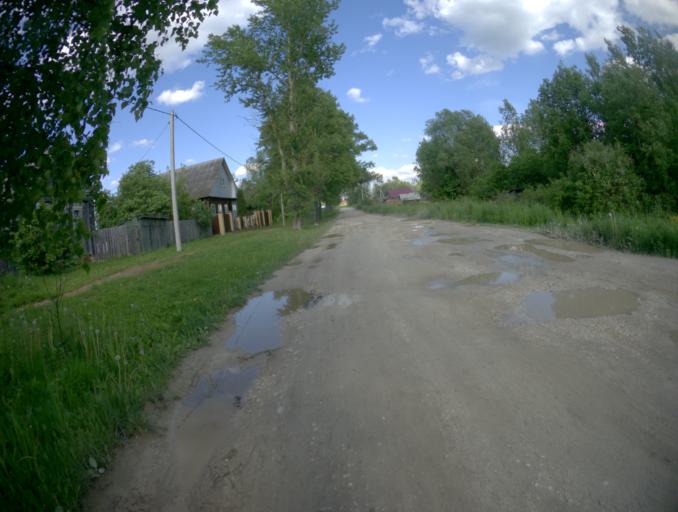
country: RU
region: Vladimir
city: Zolotkovo
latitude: 55.3320
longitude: 41.0151
